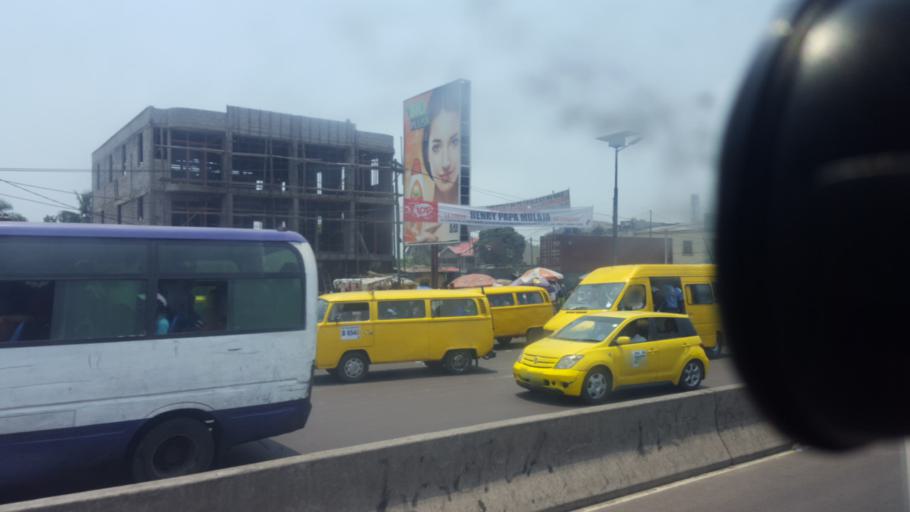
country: CD
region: Kinshasa
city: Masina
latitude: -4.3849
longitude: 15.3597
